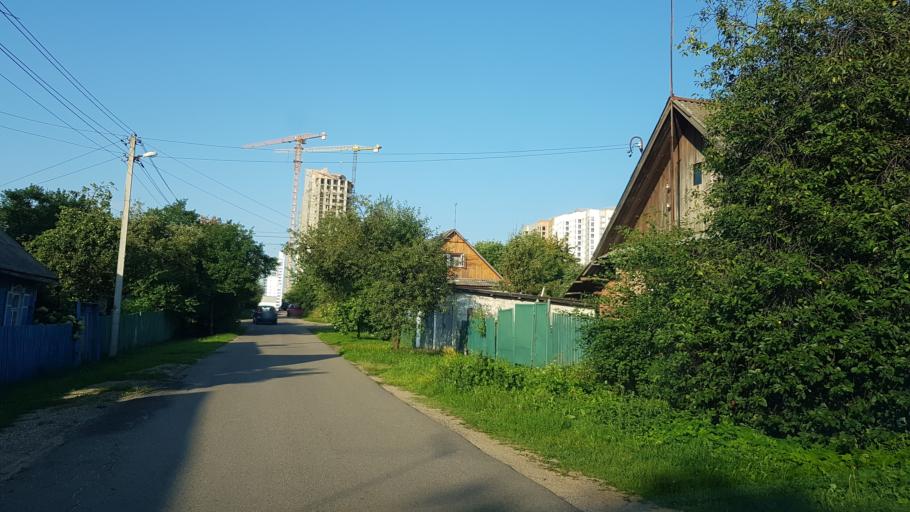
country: BY
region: Minsk
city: Minsk
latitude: 53.8861
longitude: 27.5107
